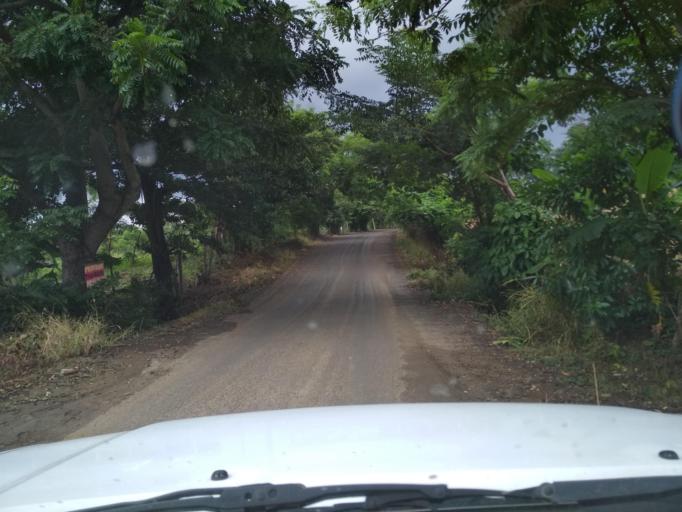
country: MX
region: Veracruz
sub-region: San Andres Tuxtla
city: El Huidero
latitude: 18.3811
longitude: -95.1773
